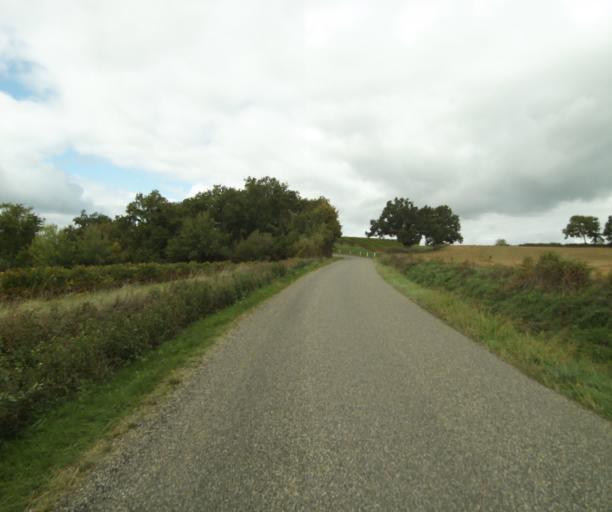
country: FR
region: Midi-Pyrenees
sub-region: Departement du Gers
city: Nogaro
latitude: 43.8255
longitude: -0.0275
